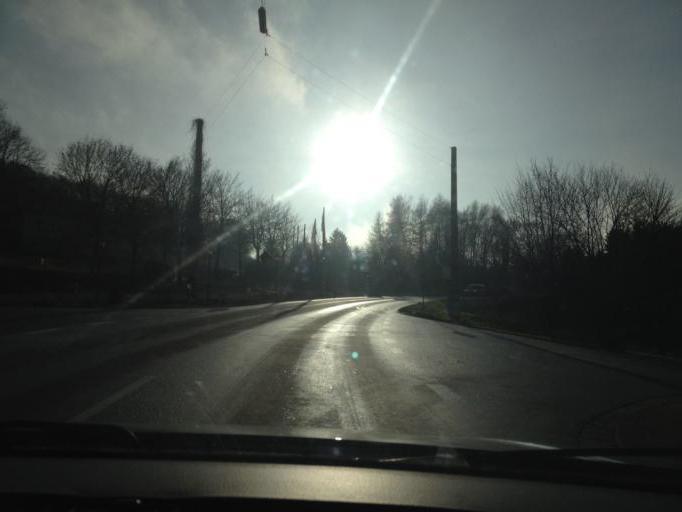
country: DE
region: Saarland
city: Marpingen
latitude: 49.4463
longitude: 7.0581
